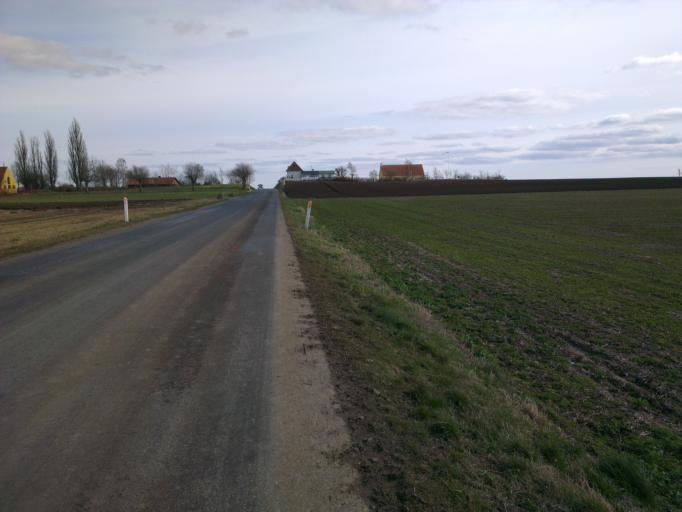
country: DK
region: Capital Region
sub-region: Frederikssund Kommune
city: Skibby
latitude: 55.7486
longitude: 11.9821
